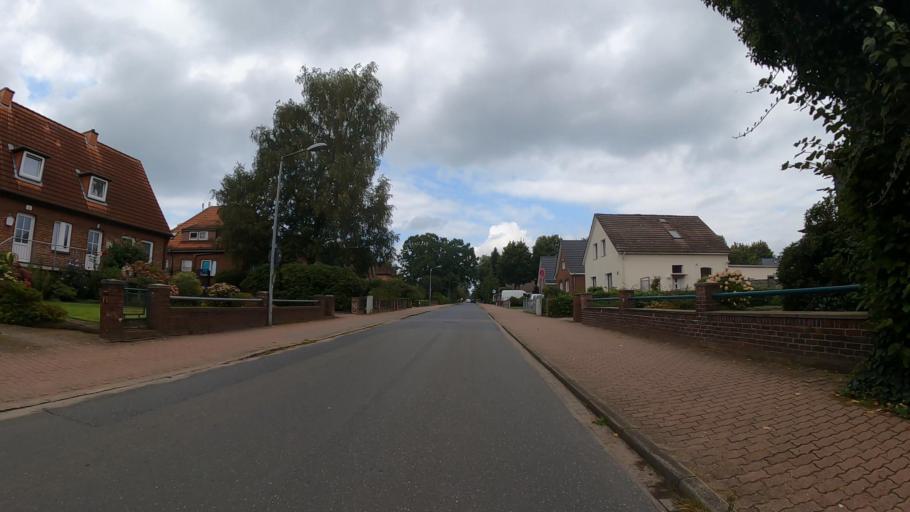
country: DE
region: Schleswig-Holstein
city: Tornesch
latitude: 53.6988
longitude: 9.7177
